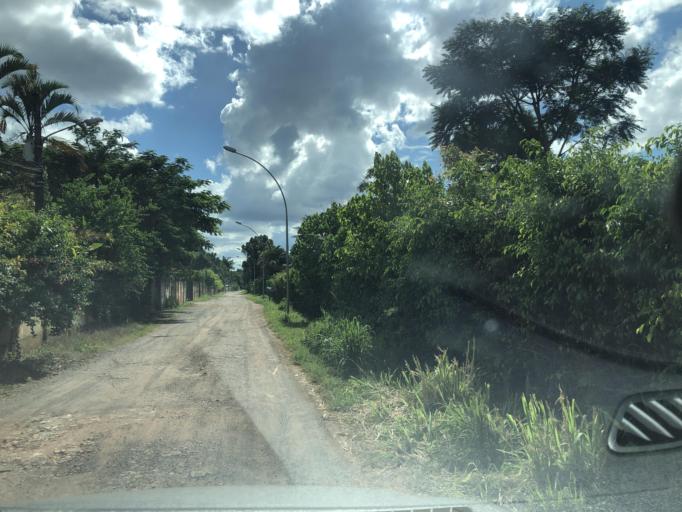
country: BR
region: Federal District
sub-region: Brasilia
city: Brasilia
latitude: -15.8760
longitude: -47.9703
